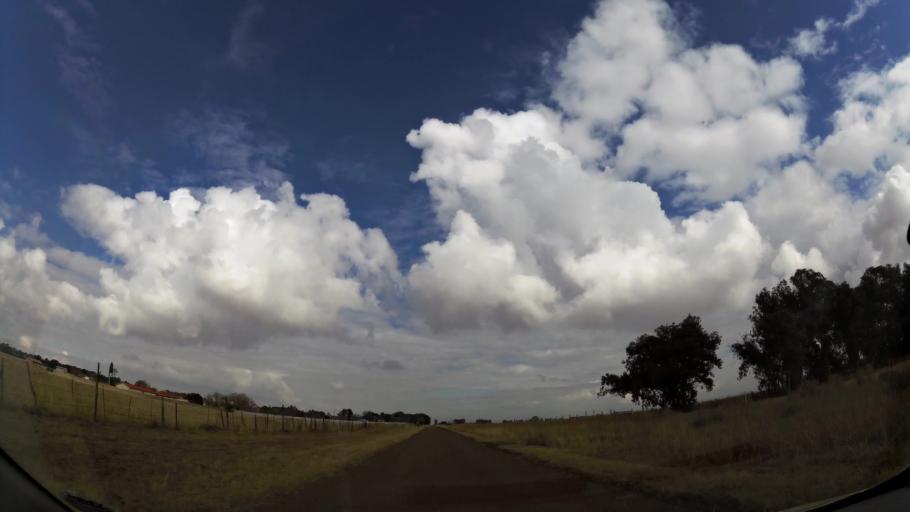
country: ZA
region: Gauteng
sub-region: Sedibeng District Municipality
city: Meyerton
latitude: -26.5974
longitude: 28.0879
